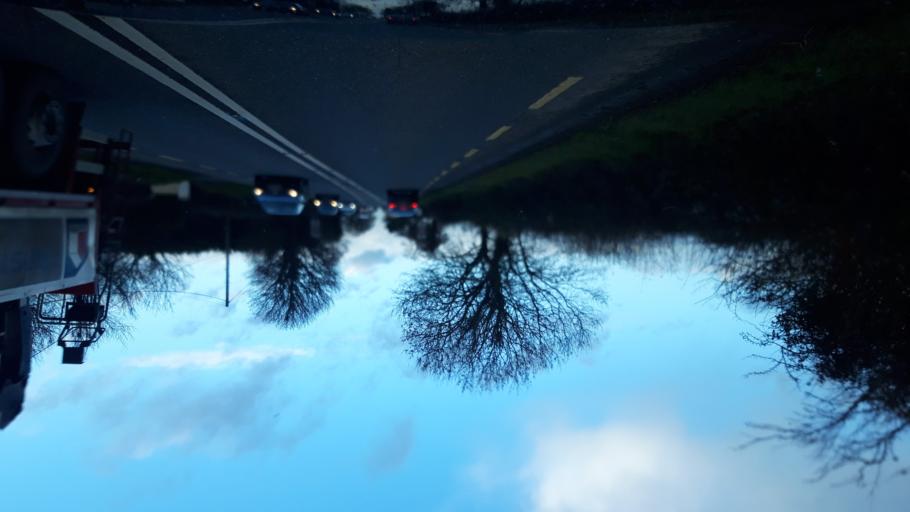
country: IE
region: Leinster
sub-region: An Mhi
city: Ratoath
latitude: 53.5509
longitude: -6.4348
